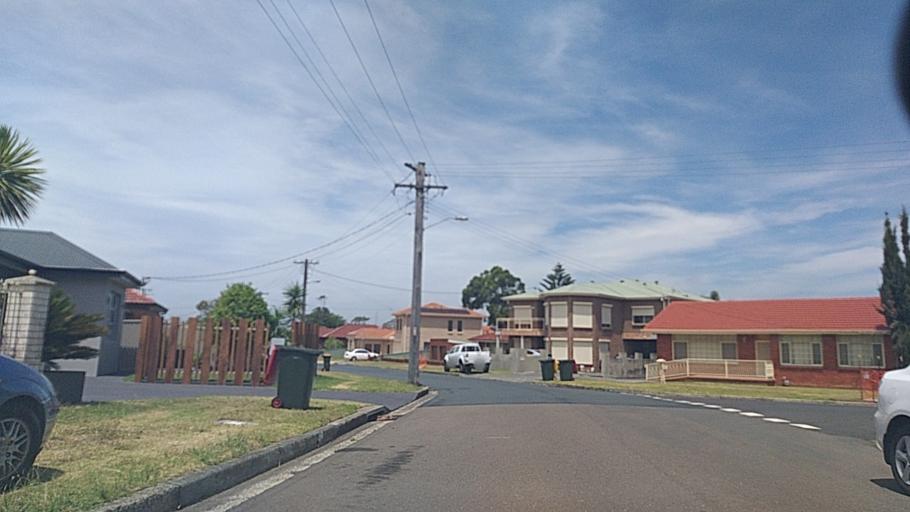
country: AU
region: New South Wales
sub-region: Wollongong
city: Fairy Meadow
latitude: -34.3926
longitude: 150.8858
